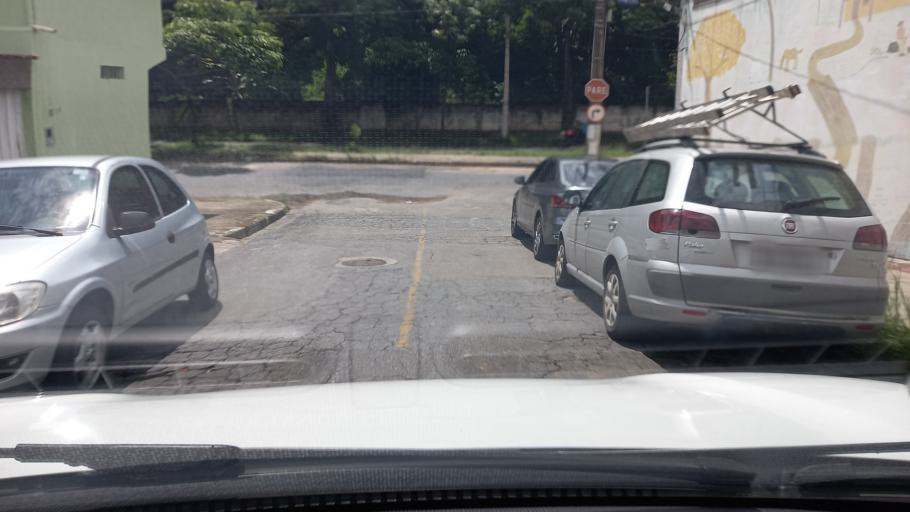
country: BR
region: Minas Gerais
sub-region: Contagem
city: Contagem
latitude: -19.8987
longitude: -44.0178
